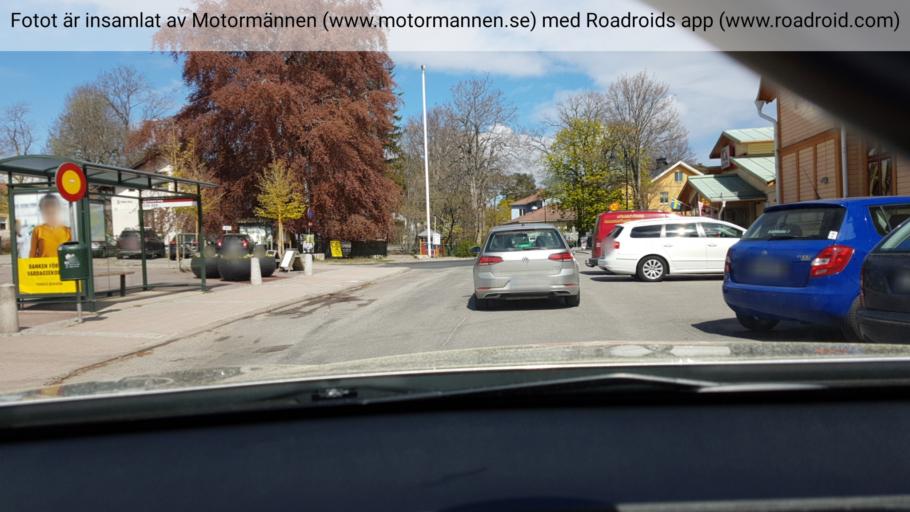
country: SE
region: Stockholm
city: Dalaro
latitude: 59.1336
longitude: 18.4086
